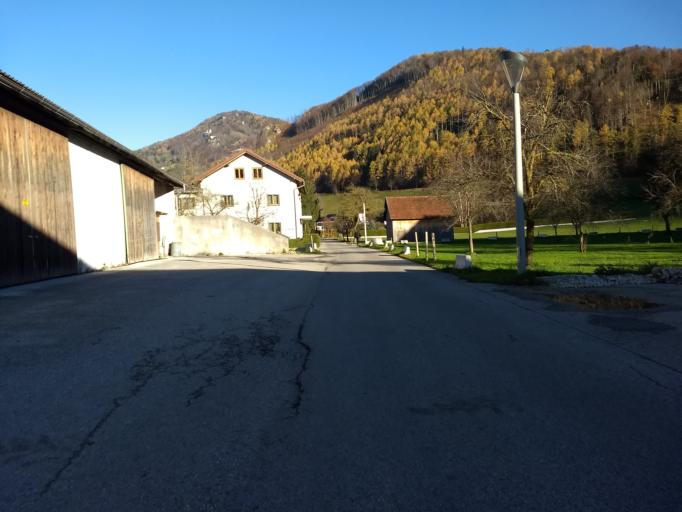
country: AT
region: Upper Austria
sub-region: Politischer Bezirk Kirchdorf an der Krems
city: Micheldorf in Oberoesterreich
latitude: 47.8777
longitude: 14.1346
